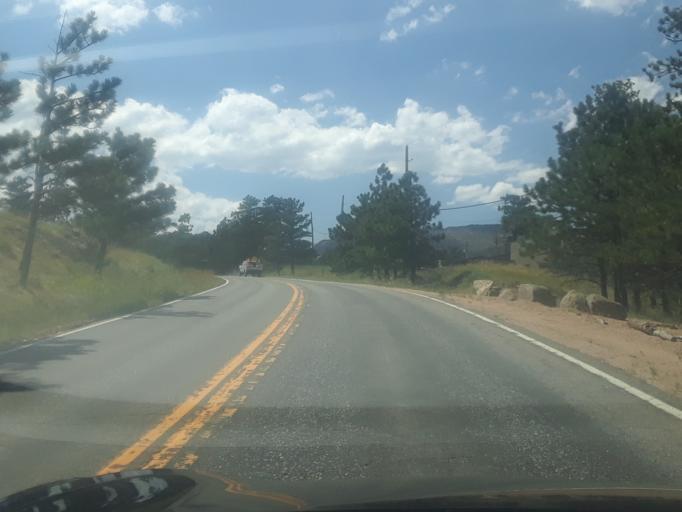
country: US
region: Colorado
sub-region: Boulder County
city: Boulder
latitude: 40.0537
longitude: -105.3567
